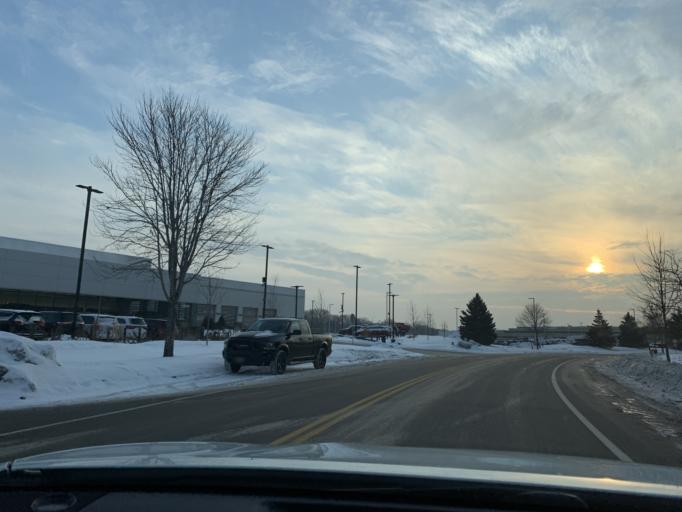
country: US
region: Minnesota
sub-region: Anoka County
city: Coon Rapids
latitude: 45.1609
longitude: -93.2862
